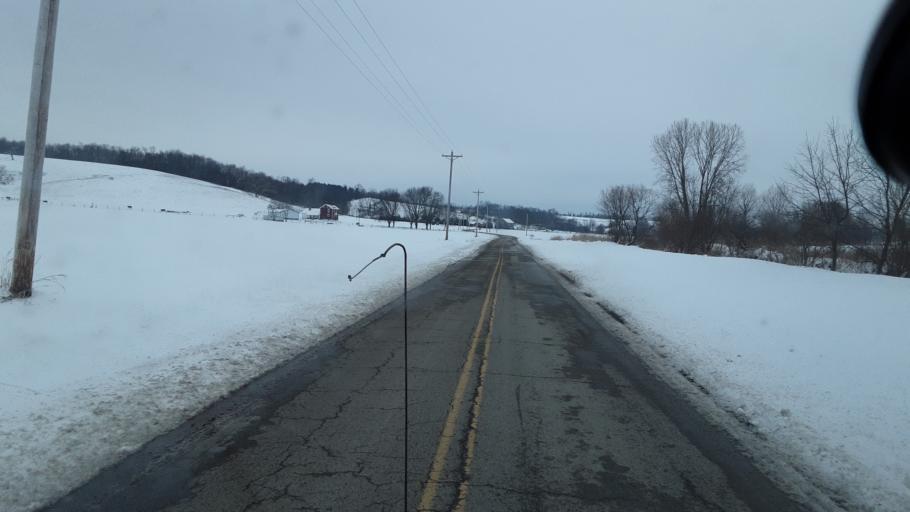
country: US
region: Ohio
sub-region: Perry County
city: Somerset
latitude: 39.8864
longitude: -82.2173
